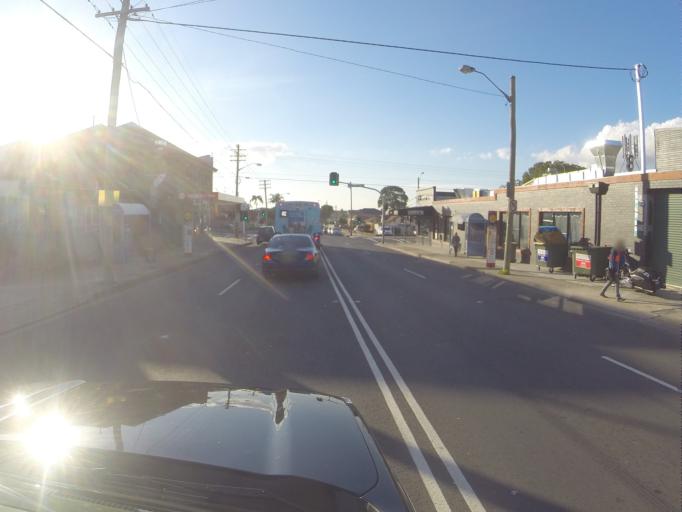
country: AU
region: New South Wales
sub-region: Rockdale
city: Bexley North
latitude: -33.9283
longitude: 151.1090
